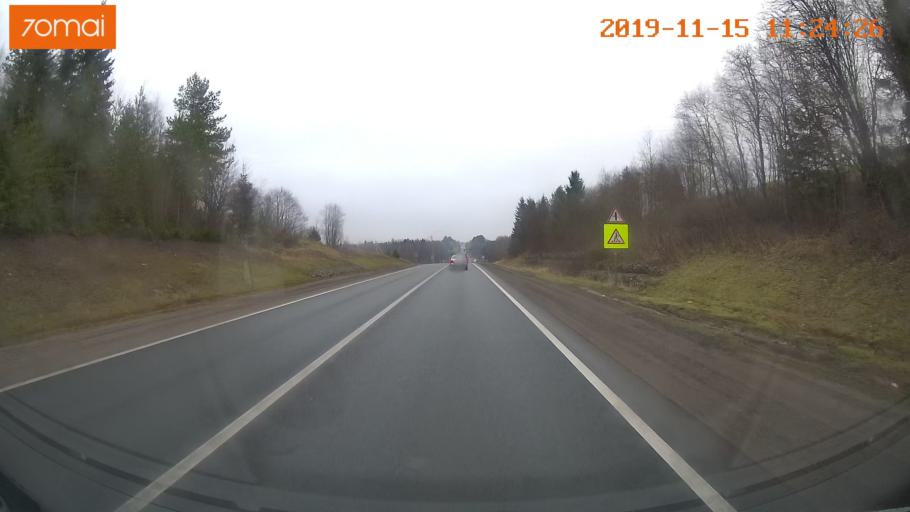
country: RU
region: Vologda
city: Molochnoye
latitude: 59.1571
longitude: 39.4049
